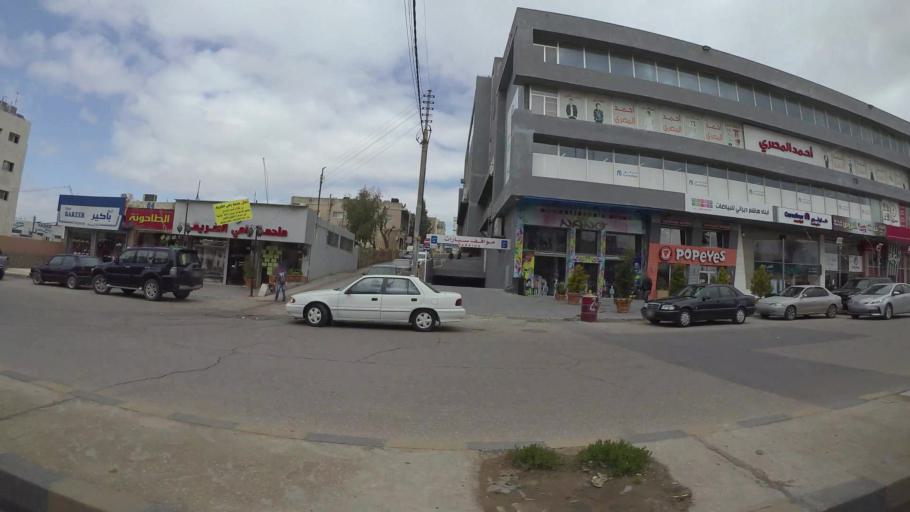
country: JO
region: Amman
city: Wadi as Sir
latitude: 31.9541
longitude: 35.8359
